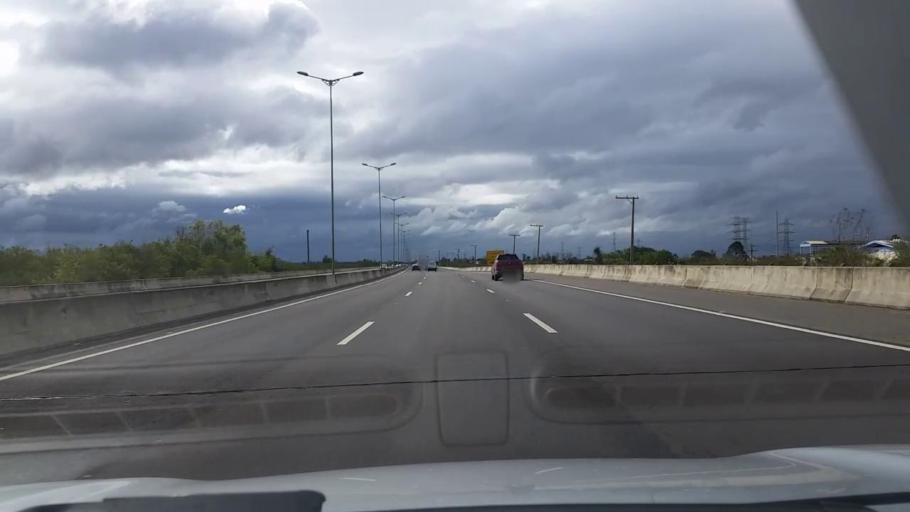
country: BR
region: Rio Grande do Sul
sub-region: Canoas
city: Canoas
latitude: -29.9554
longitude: -51.2024
